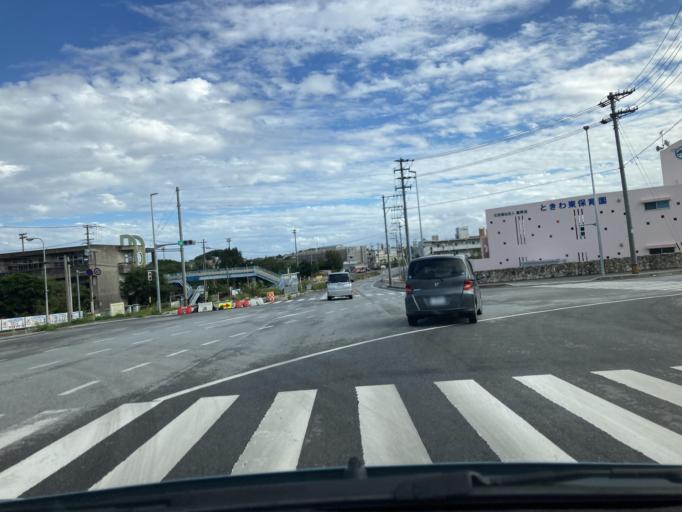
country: JP
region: Okinawa
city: Tomigusuku
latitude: 26.1518
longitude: 127.7220
